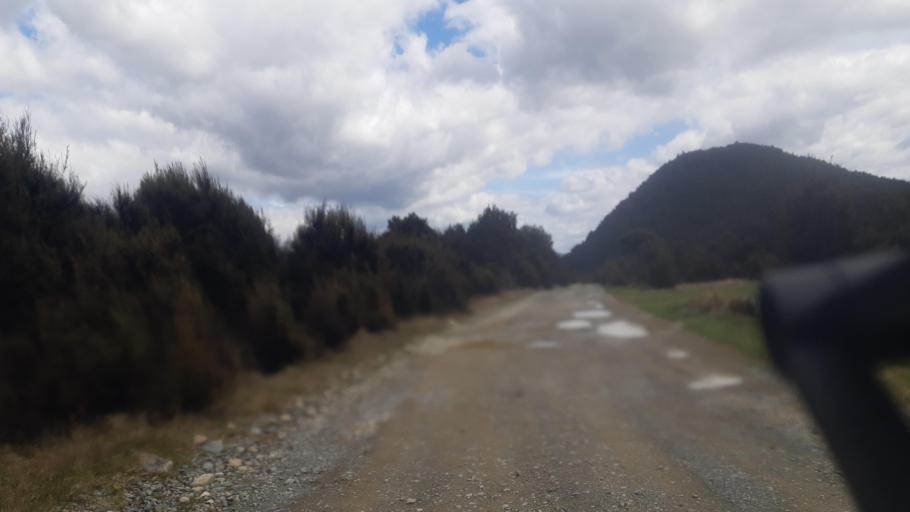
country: NZ
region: Tasman
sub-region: Tasman District
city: Wakefield
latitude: -41.7859
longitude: 172.8208
